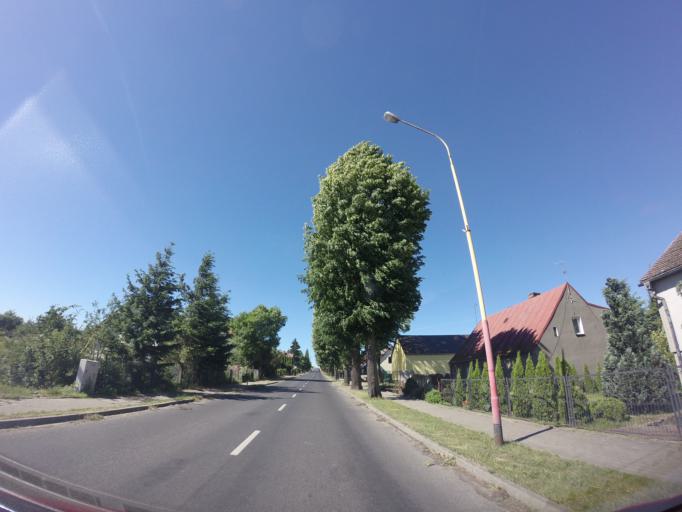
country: PL
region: West Pomeranian Voivodeship
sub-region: Powiat stargardzki
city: Dolice
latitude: 53.1882
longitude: 15.2000
